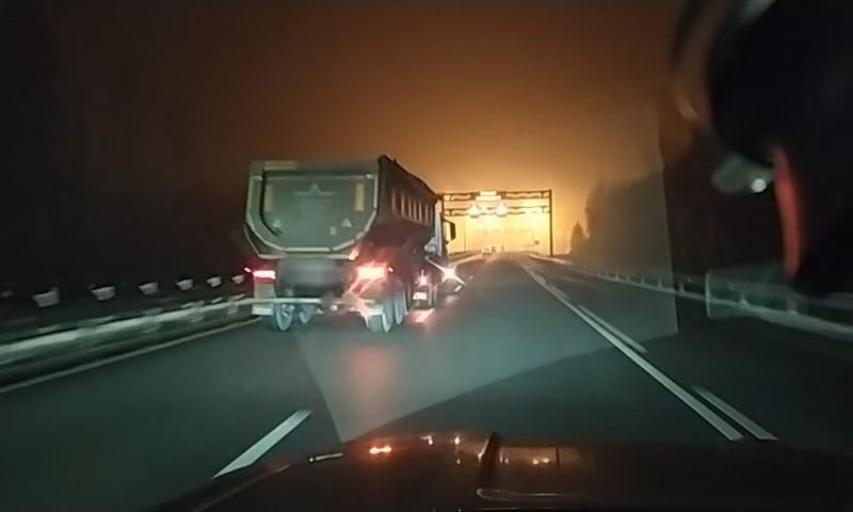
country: RU
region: Leningrad
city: Agalatovo
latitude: 60.2158
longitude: 30.3598
